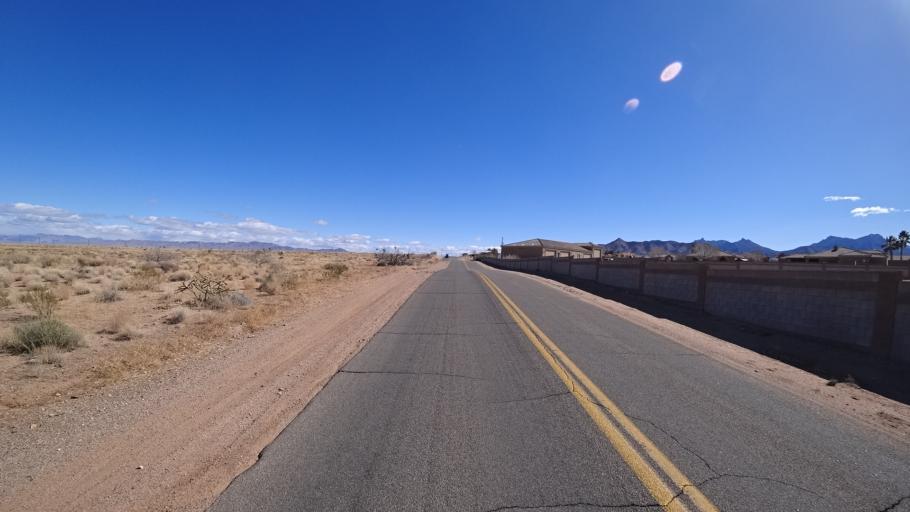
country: US
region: Arizona
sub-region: Mohave County
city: Kingman
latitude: 35.1958
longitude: -113.9954
